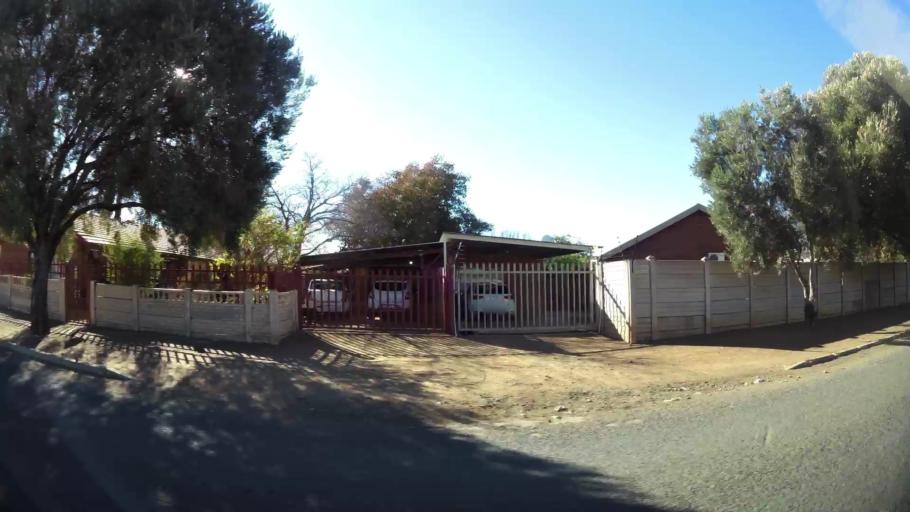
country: ZA
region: Northern Cape
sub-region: Frances Baard District Municipality
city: Kimberley
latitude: -28.7430
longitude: 24.7916
